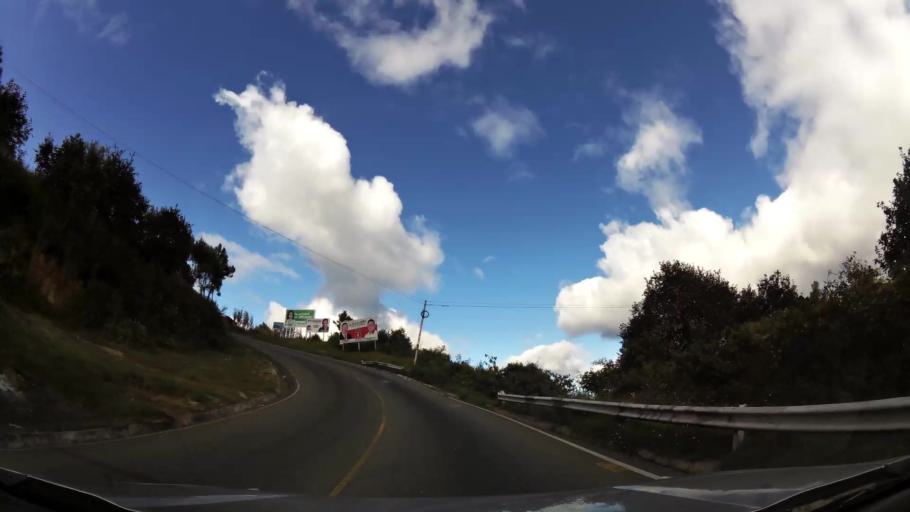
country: GT
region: Quiche
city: Chichicastenango
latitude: 14.9236
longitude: -91.1037
